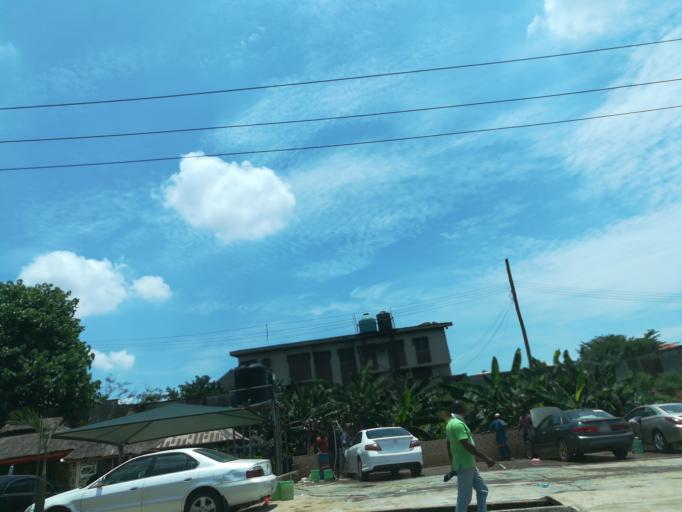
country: NG
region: Lagos
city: Ebute Ikorodu
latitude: 6.6060
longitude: 3.4961
